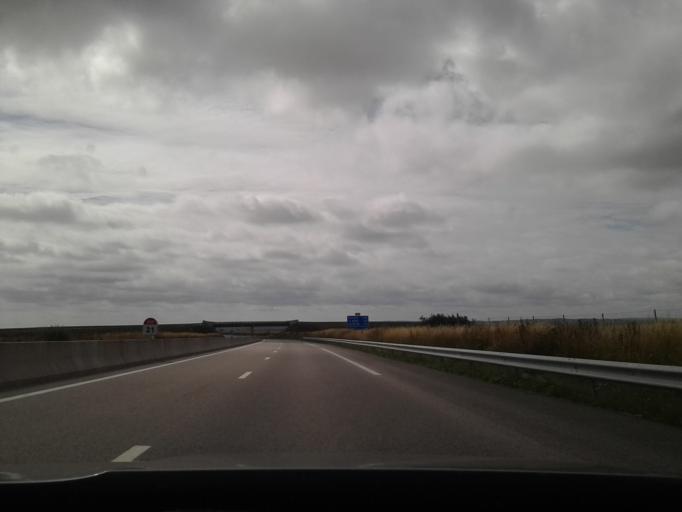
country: FR
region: Lower Normandy
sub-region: Departement de l'Orne
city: Argentan
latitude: 48.7126
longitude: -0.0545
